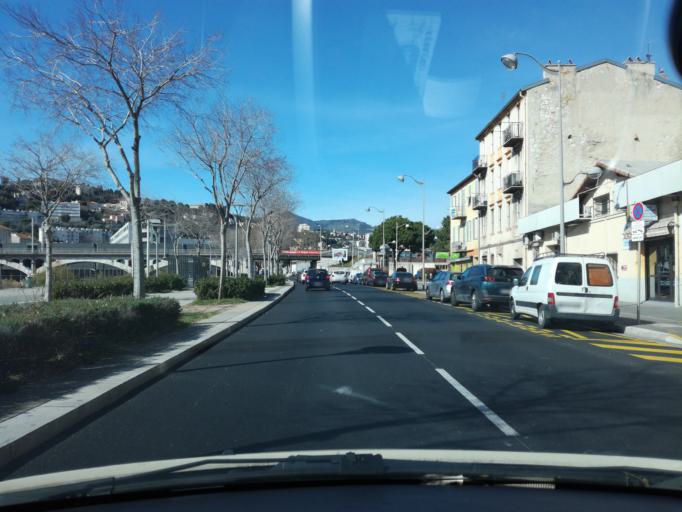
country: FR
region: Provence-Alpes-Cote d'Azur
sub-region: Departement des Alpes-Maritimes
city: Saint-Andre-de-la-Roche
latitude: 43.7132
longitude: 7.2839
